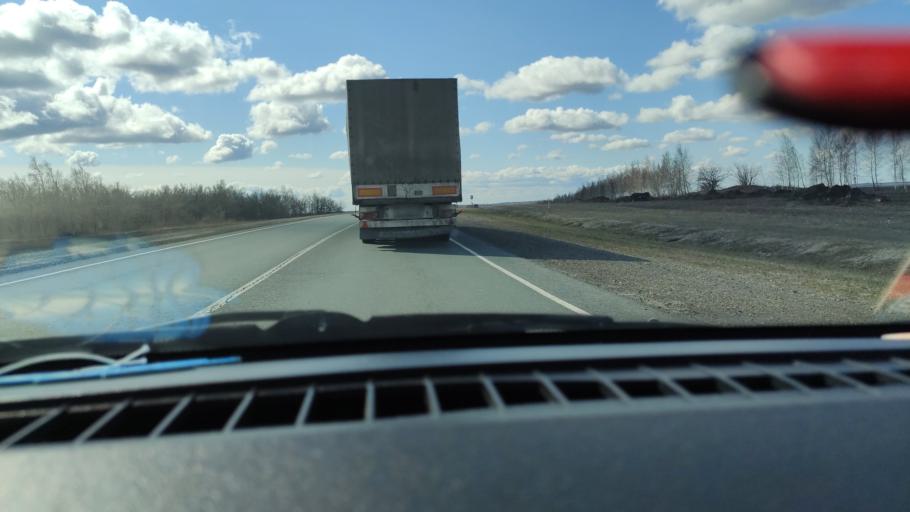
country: RU
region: Samara
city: Syzran'
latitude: 52.9300
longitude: 48.3062
